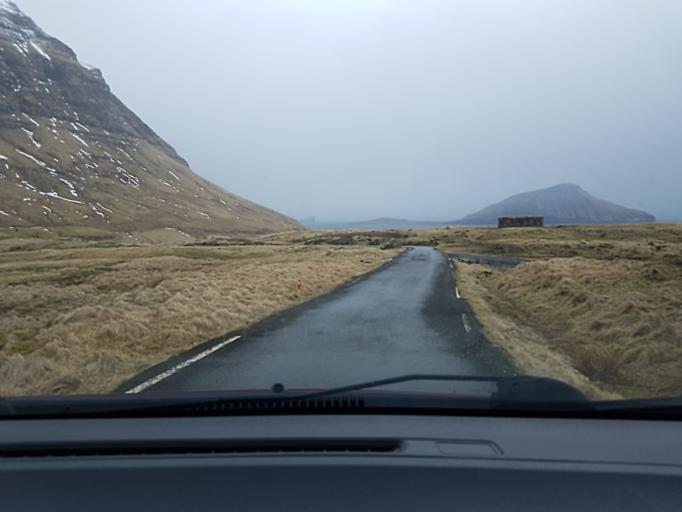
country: FO
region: Streymoy
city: Kollafjordhur
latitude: 62.0442
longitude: -6.9266
